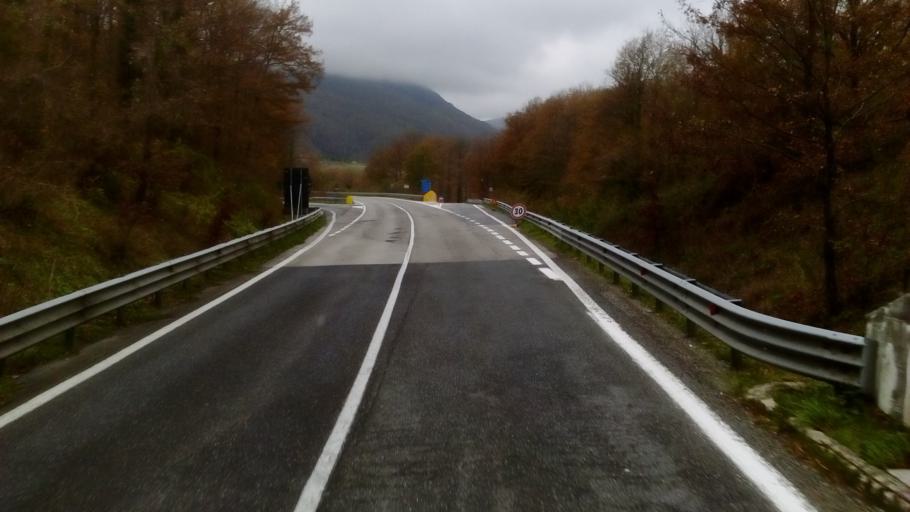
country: IT
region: Molise
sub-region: Provincia di Isernia
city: Pescolanciano
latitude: 41.6729
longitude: 14.3559
